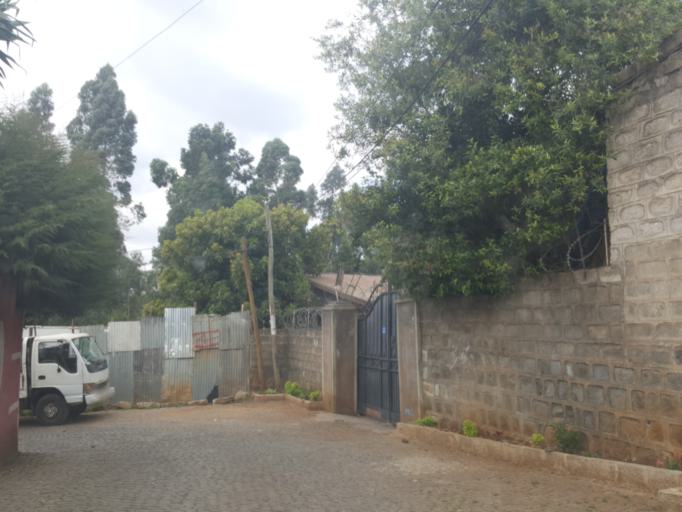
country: ET
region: Adis Abeba
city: Addis Ababa
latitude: 9.0603
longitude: 38.7181
